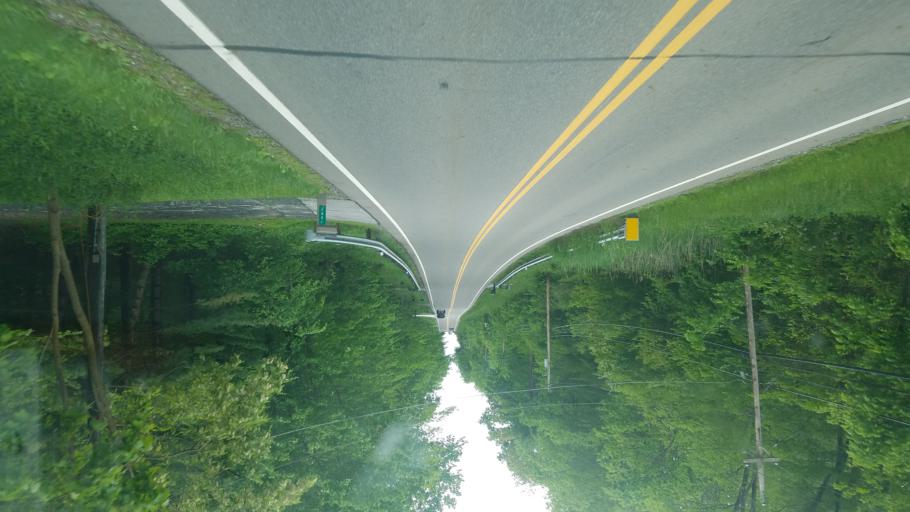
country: US
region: Ohio
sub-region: Geauga County
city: Bainbridge
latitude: 41.3620
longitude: -81.3565
